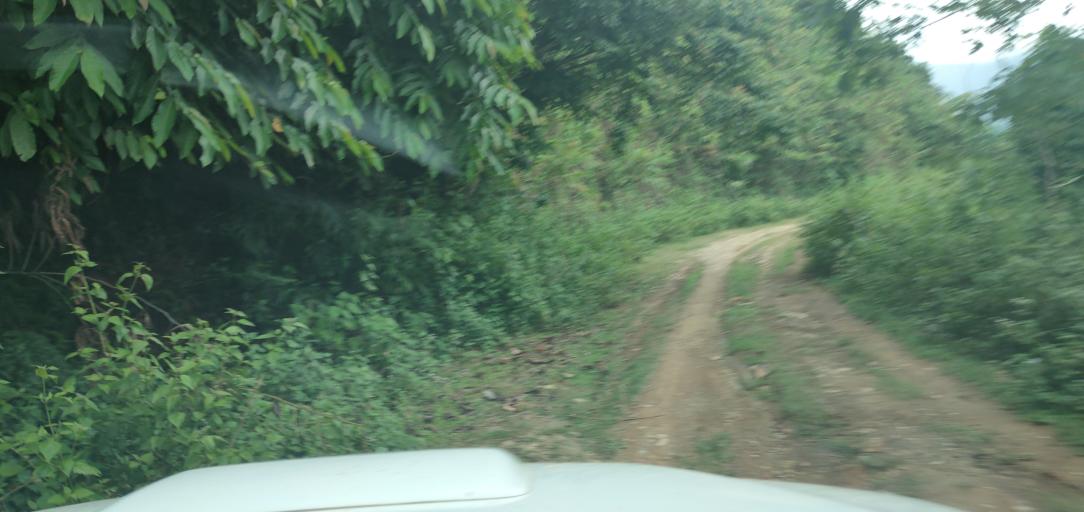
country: LA
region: Phongsali
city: Phongsali
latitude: 21.4411
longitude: 102.3238
